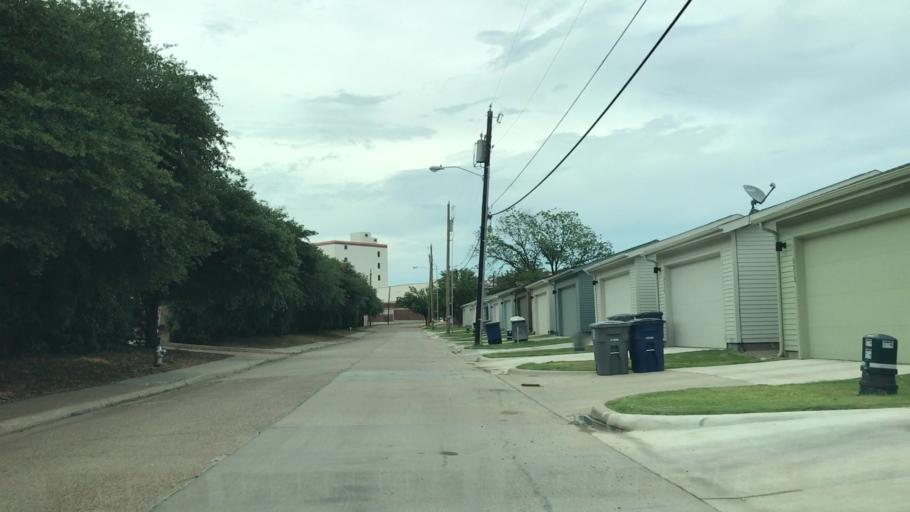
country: US
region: Texas
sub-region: Dallas County
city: Highland Park
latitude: 32.8343
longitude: -96.7782
